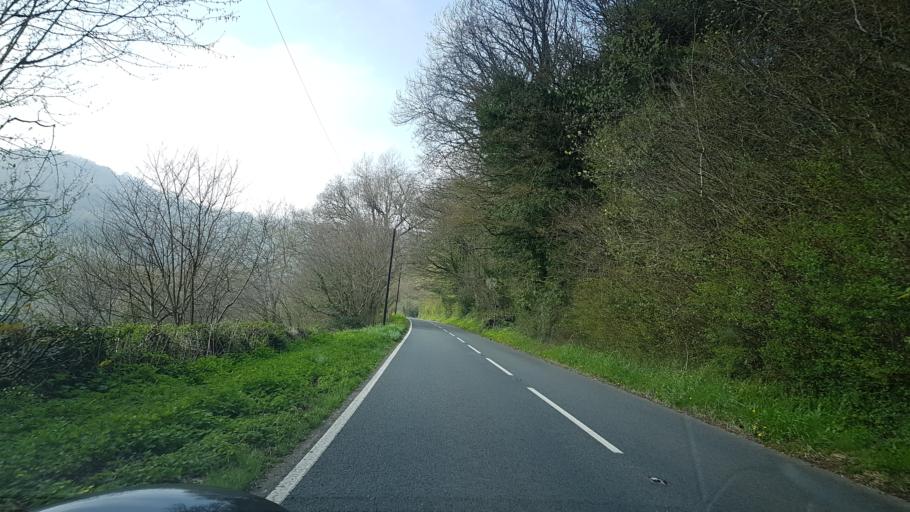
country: GB
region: England
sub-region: Gloucestershire
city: Coleford
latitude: 51.7588
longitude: -2.6652
